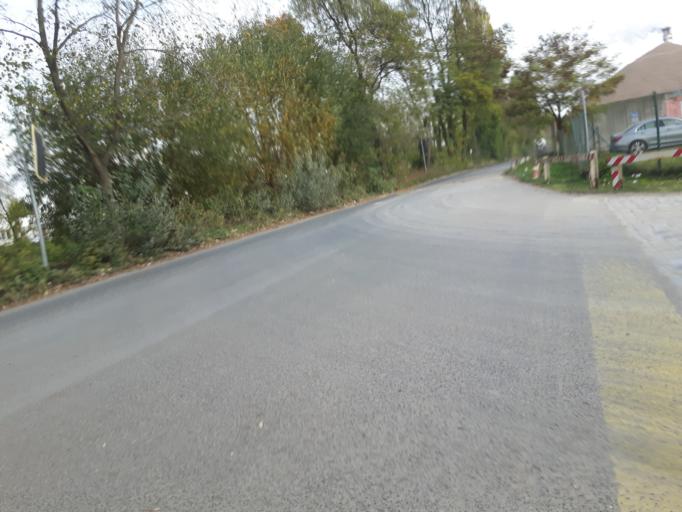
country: DE
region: Berlin
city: Haselhorst
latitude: 52.5351
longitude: 13.2234
